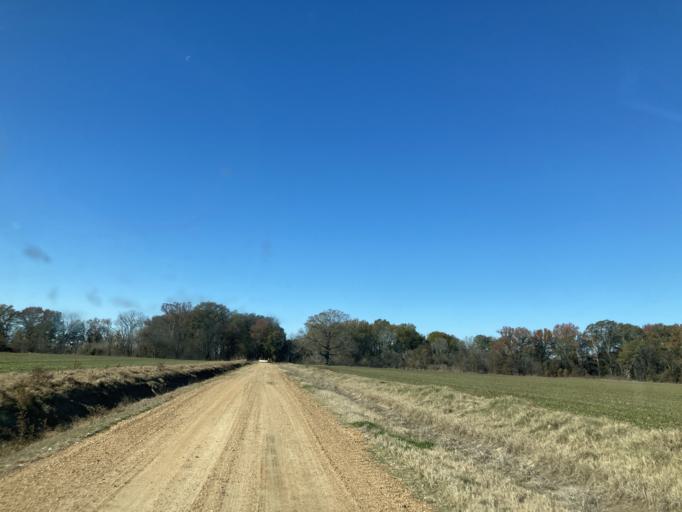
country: US
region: Mississippi
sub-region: Sharkey County
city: Rolling Fork
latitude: 32.8498
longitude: -90.6933
